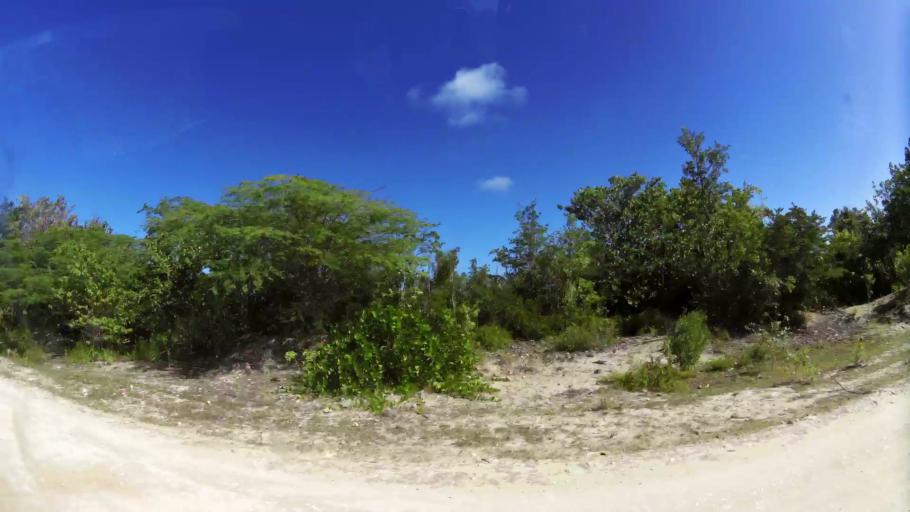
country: AG
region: Barbuda
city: Codrington
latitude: 17.5964
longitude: -61.8292
